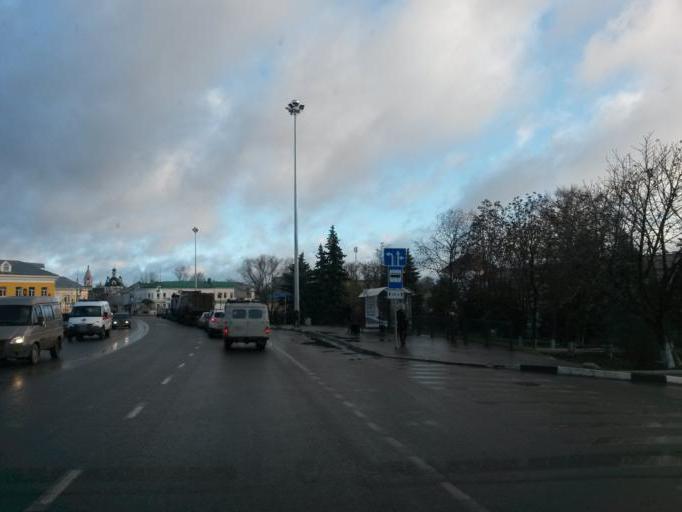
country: RU
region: Jaroslavl
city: Pereslavl'-Zalesskiy
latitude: 56.7376
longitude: 38.8552
